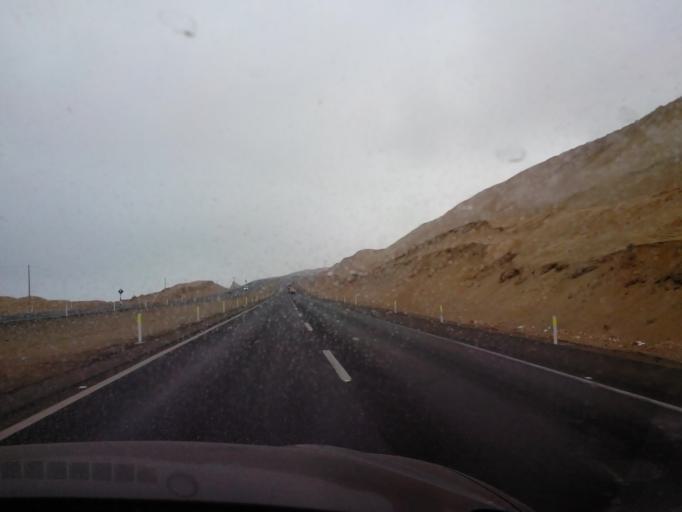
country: PE
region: Ica
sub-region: Provincia de Chincha
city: San Pedro
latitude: -13.3067
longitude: -76.2521
